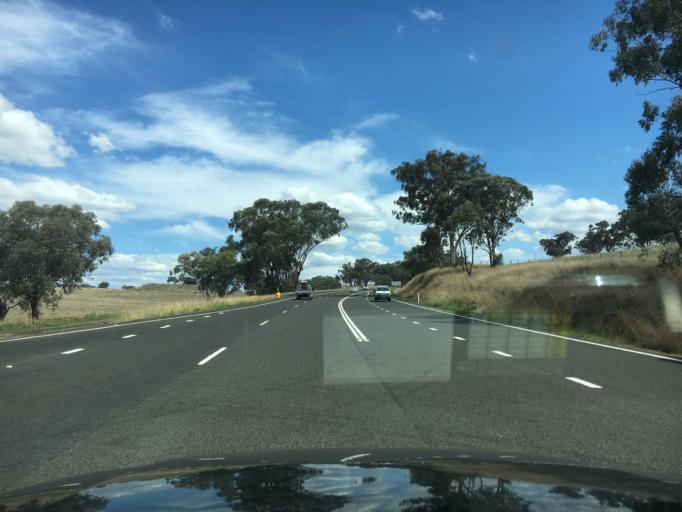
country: AU
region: New South Wales
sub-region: Liverpool Plains
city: Quirindi
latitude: -31.4944
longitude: 150.8647
